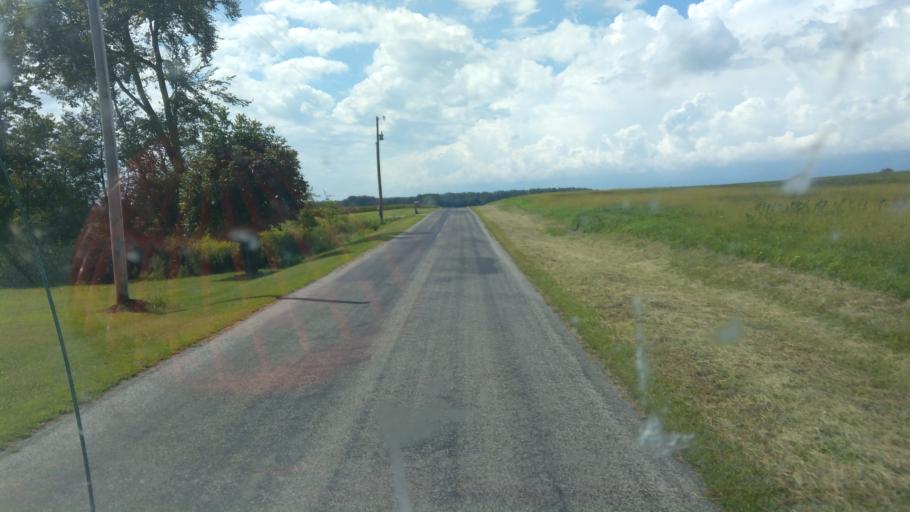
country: US
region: Ohio
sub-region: Union County
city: Richwood
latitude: 40.6001
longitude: -83.4005
